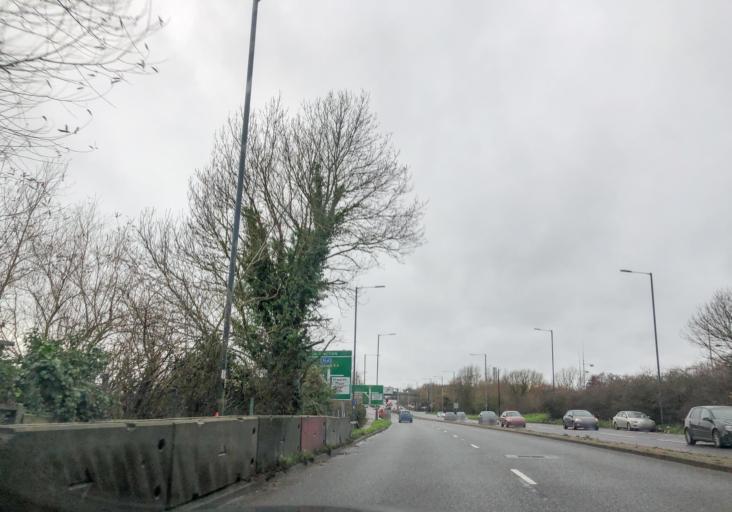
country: GB
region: England
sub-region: Buckinghamshire
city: Iver
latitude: 51.4834
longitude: -0.4883
